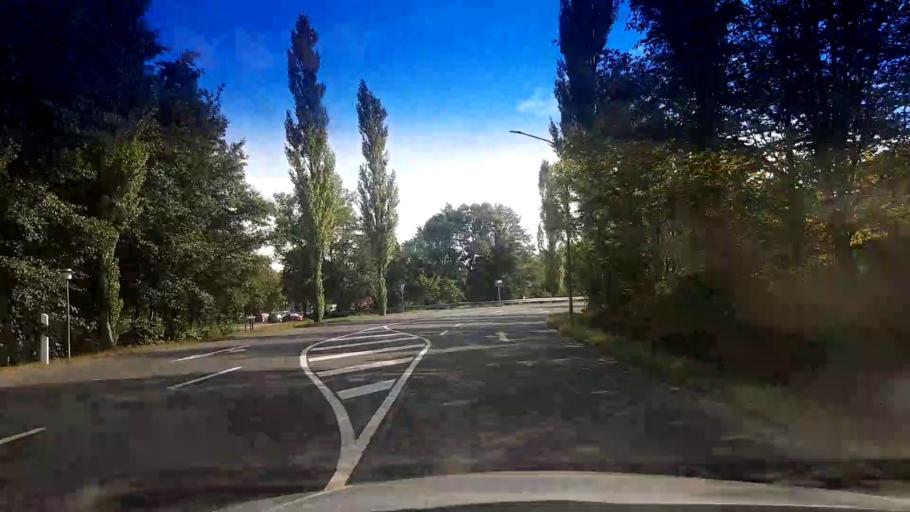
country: DE
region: Bavaria
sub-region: Upper Palatinate
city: Tirschenreuth
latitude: 49.8781
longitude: 12.3332
